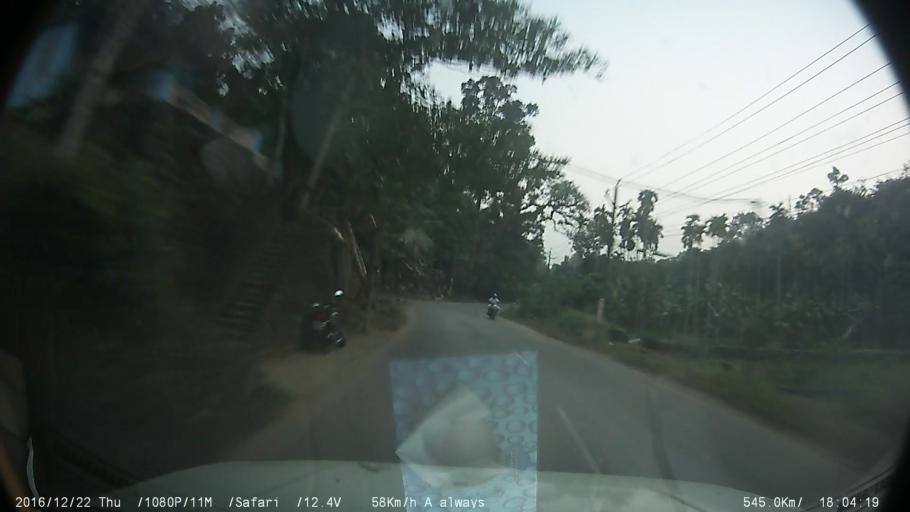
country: IN
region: Kerala
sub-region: Kottayam
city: Palackattumala
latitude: 9.8369
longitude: 76.6069
